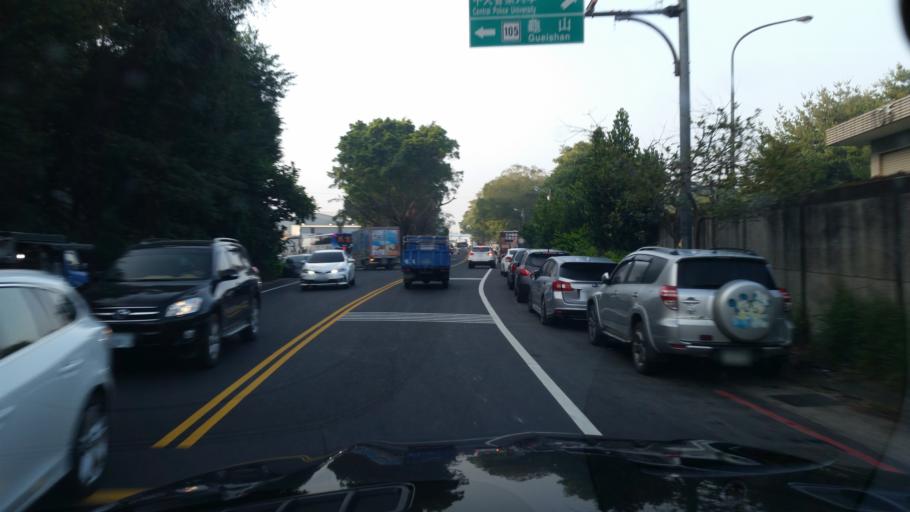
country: TW
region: Taiwan
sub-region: Taoyuan
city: Taoyuan
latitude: 25.0604
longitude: 121.3582
